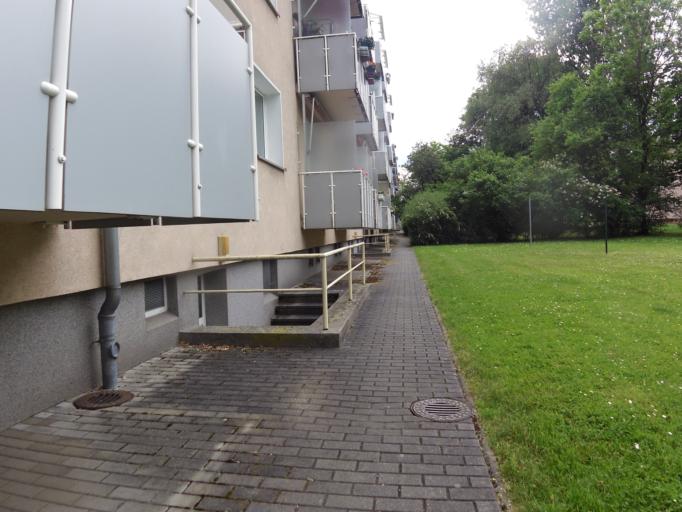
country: DE
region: Saxony
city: Leipzig
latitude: 51.3747
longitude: 12.3774
